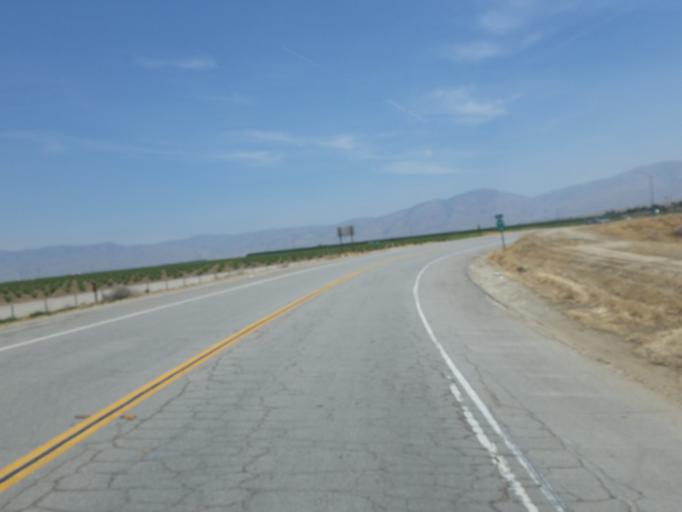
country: US
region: California
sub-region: Kern County
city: Weedpatch
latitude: 35.0566
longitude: -118.9659
